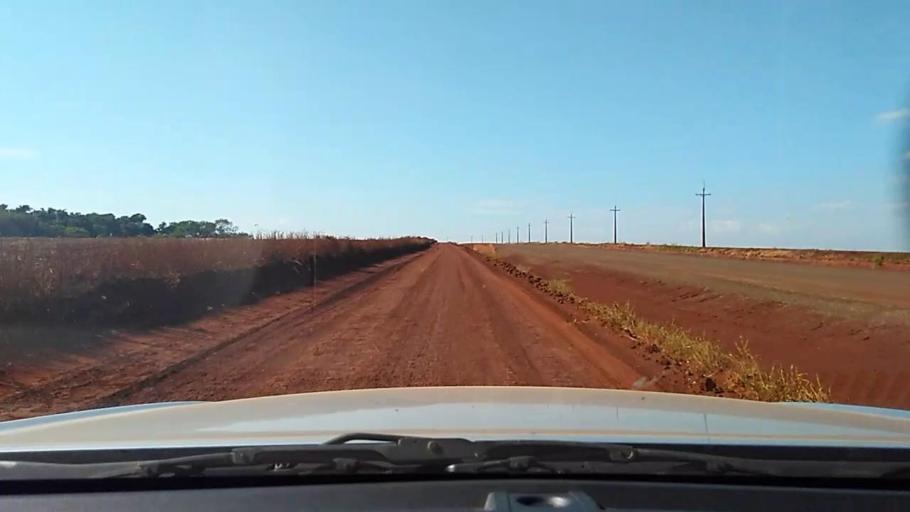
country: PY
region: Alto Parana
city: Naranjal
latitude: -25.9119
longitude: -55.4412
